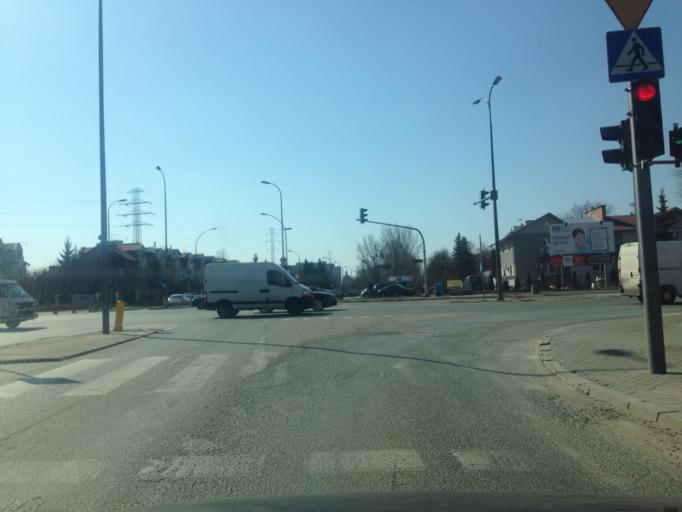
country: PL
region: Masovian Voivodeship
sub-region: Warszawa
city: Wilanow
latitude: 52.1796
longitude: 21.0724
